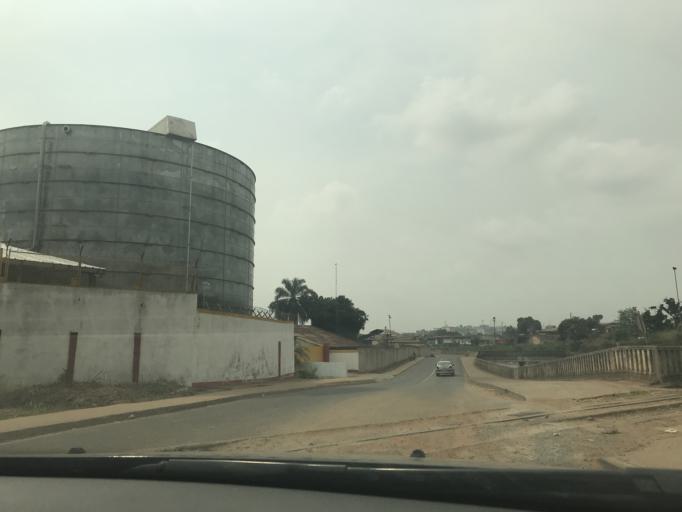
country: CM
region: Centre
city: Yaounde
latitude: 3.8407
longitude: 11.5132
